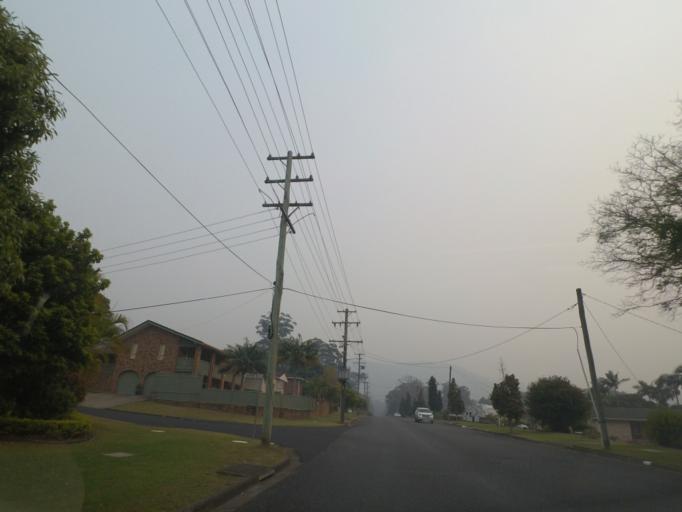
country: AU
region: New South Wales
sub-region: Coffs Harbour
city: Coffs Harbour
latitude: -30.2823
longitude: 153.1032
